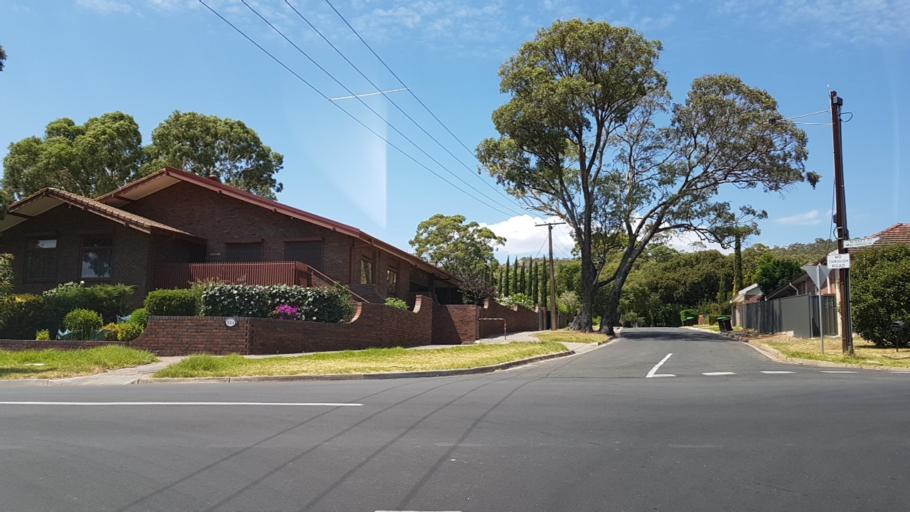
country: AU
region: South Australia
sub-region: Burnside
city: Hazelwood Park
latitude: -34.9400
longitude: 138.6657
